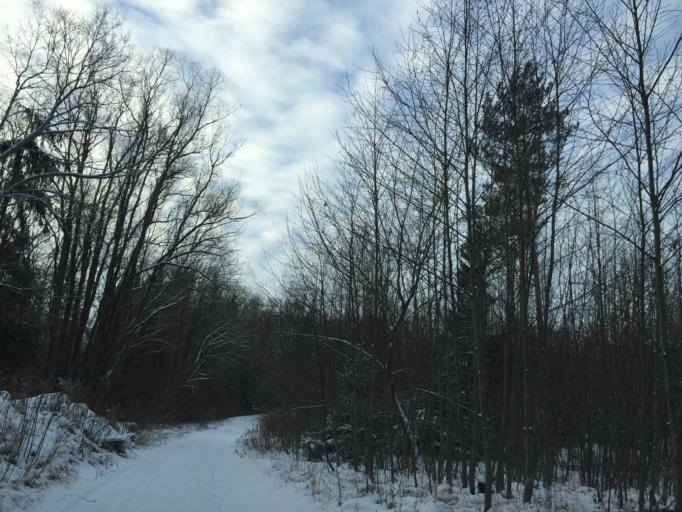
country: LV
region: Ligatne
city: Ligatne
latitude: 57.2040
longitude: 25.1529
